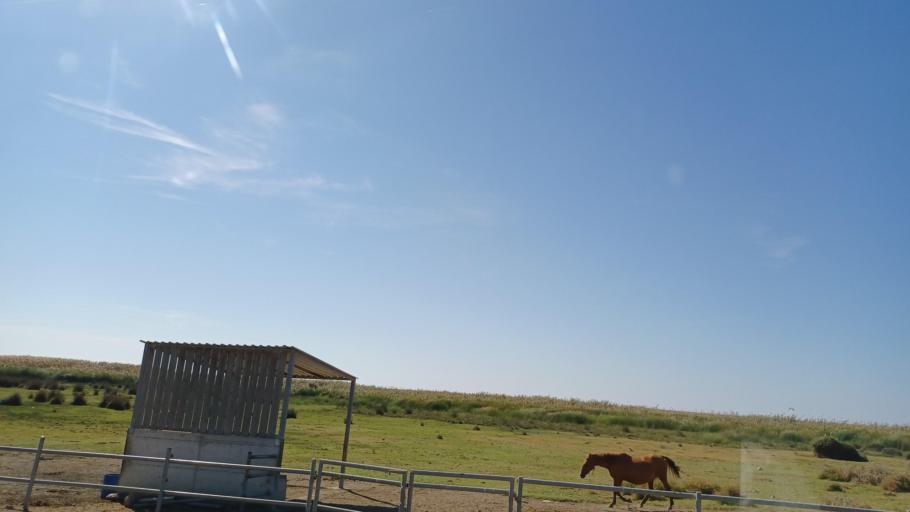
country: CY
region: Larnaka
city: Kolossi
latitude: 34.6347
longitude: 32.9270
